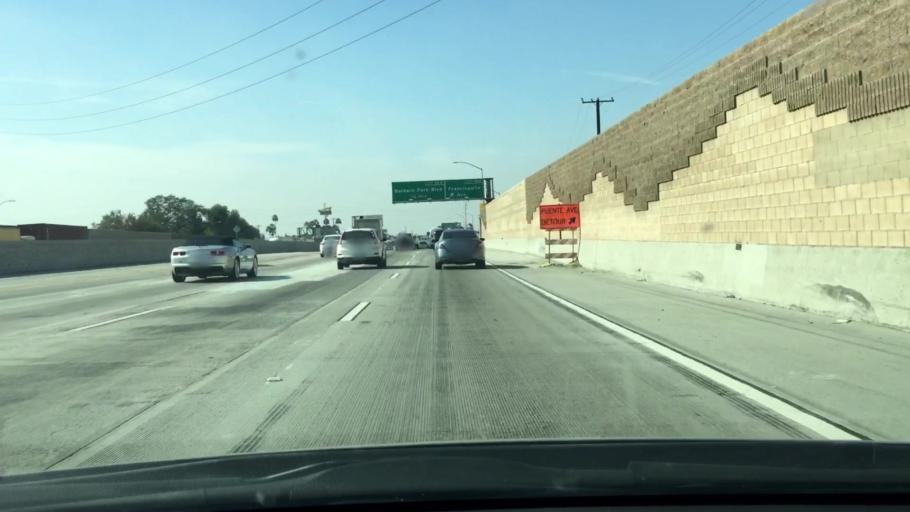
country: US
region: California
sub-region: Los Angeles County
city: Baldwin Park
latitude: 34.0695
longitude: -117.9685
